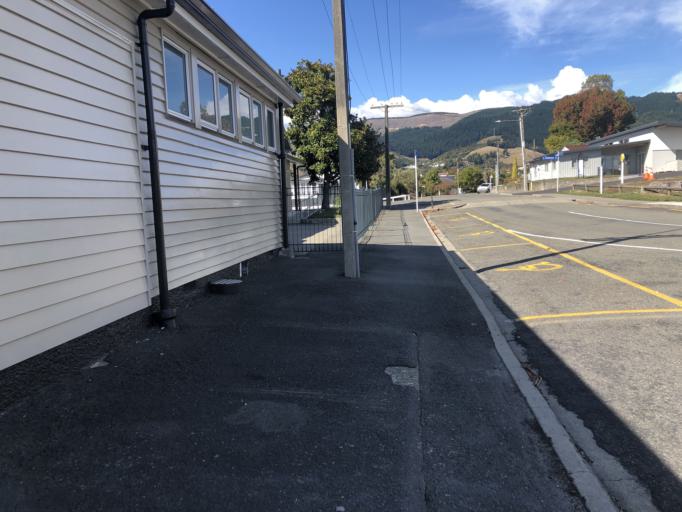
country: NZ
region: Tasman
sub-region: Tasman District
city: Richmond
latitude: -41.3395
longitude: 173.1814
